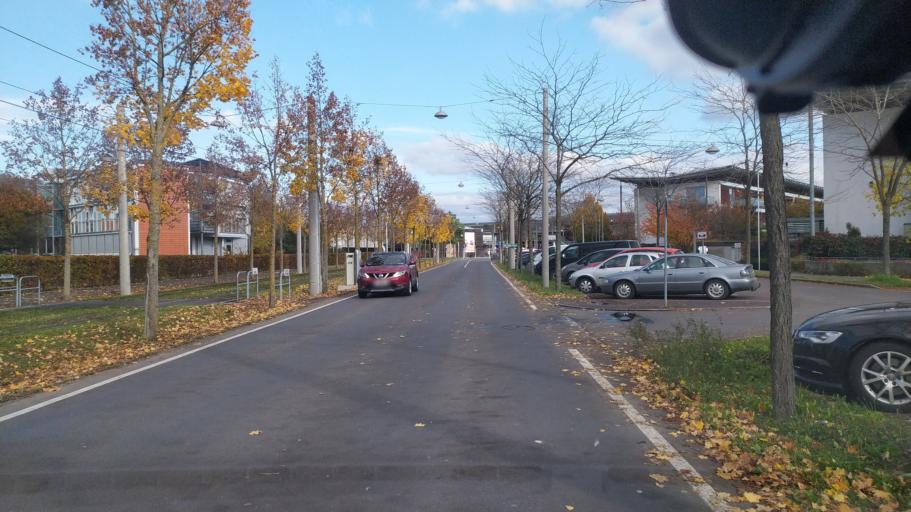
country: AT
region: Upper Austria
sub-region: Politischer Bezirk Urfahr-Umgebung
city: Steyregg
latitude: 48.2567
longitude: 14.3581
